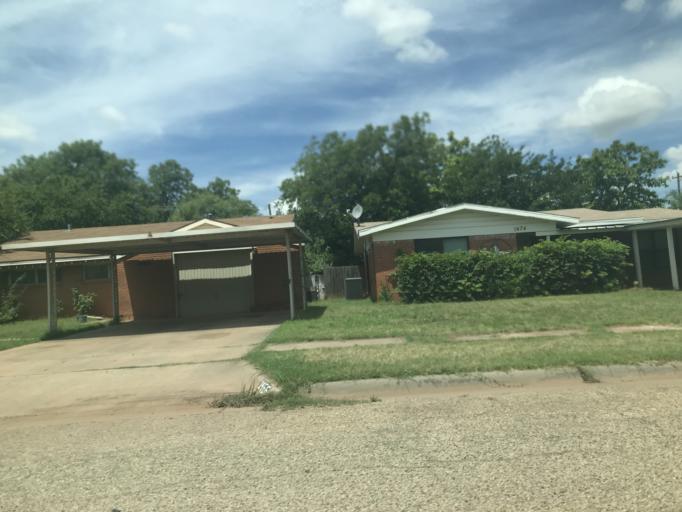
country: US
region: Texas
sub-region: Taylor County
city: Abilene
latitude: 32.4668
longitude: -99.7601
